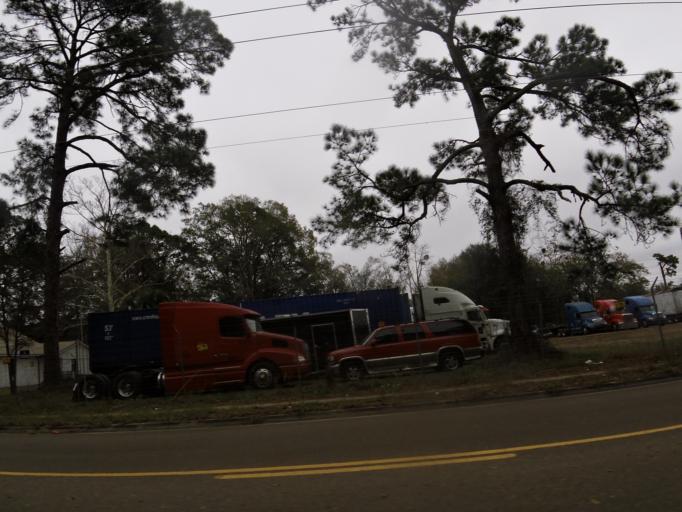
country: US
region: Florida
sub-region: Duval County
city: Jacksonville
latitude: 30.3636
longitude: -81.6988
